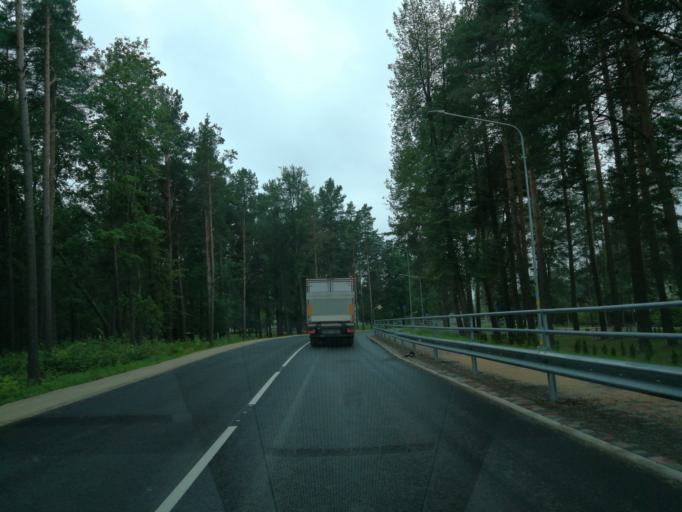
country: LV
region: Livani
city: Livani
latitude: 56.3545
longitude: 26.1835
